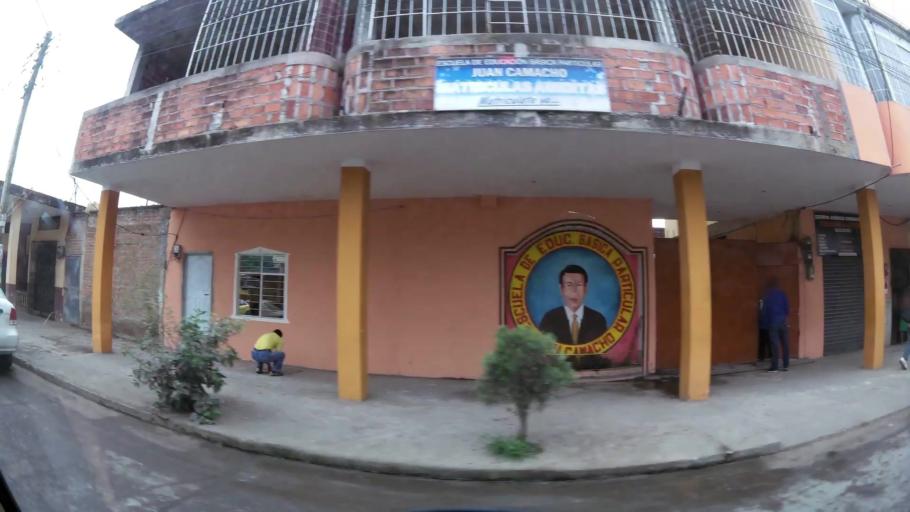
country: EC
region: El Oro
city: Pasaje
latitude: -3.3244
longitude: -79.8099
